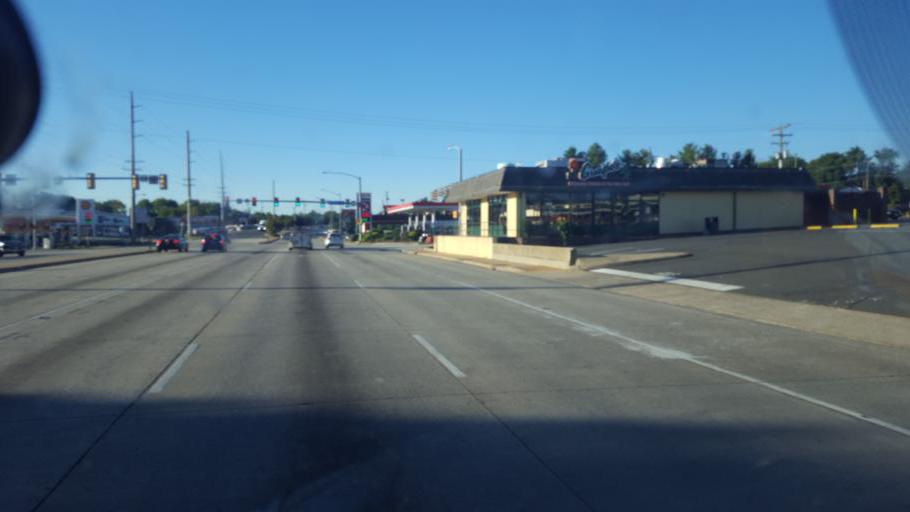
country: US
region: Virginia
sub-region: City of Manassas Park
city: Manassas Park
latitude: 38.7725
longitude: -77.4525
